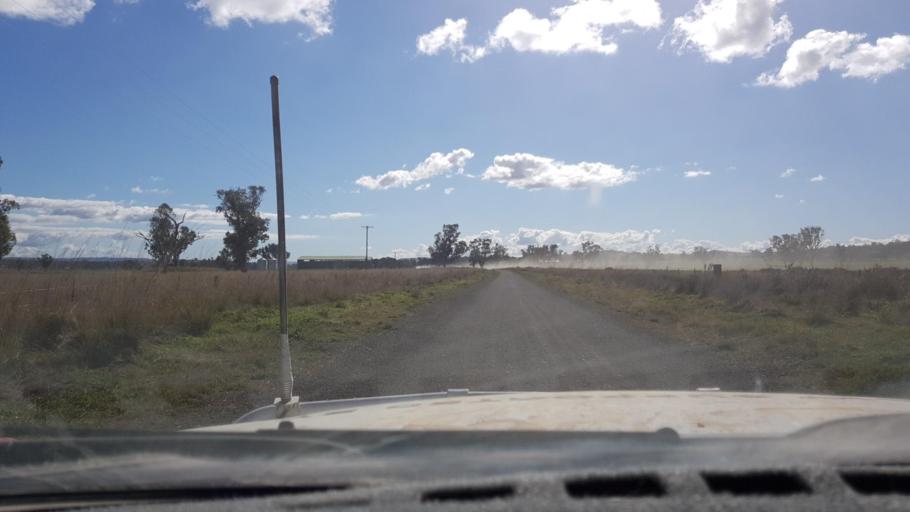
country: AU
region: New South Wales
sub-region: Narrabri
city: Blair Athol
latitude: -30.5328
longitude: 150.4419
